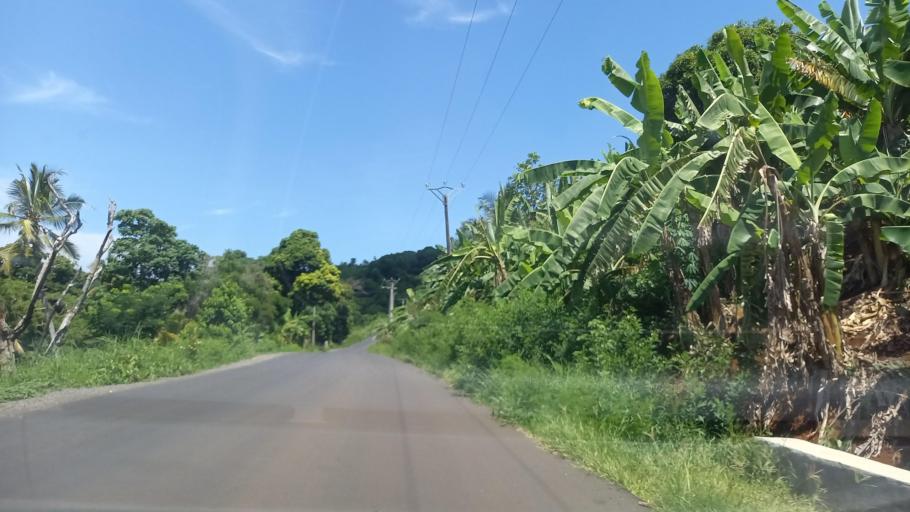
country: YT
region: M'Tsangamouji
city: M'Tsangamouji
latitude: -12.7600
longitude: 45.0706
